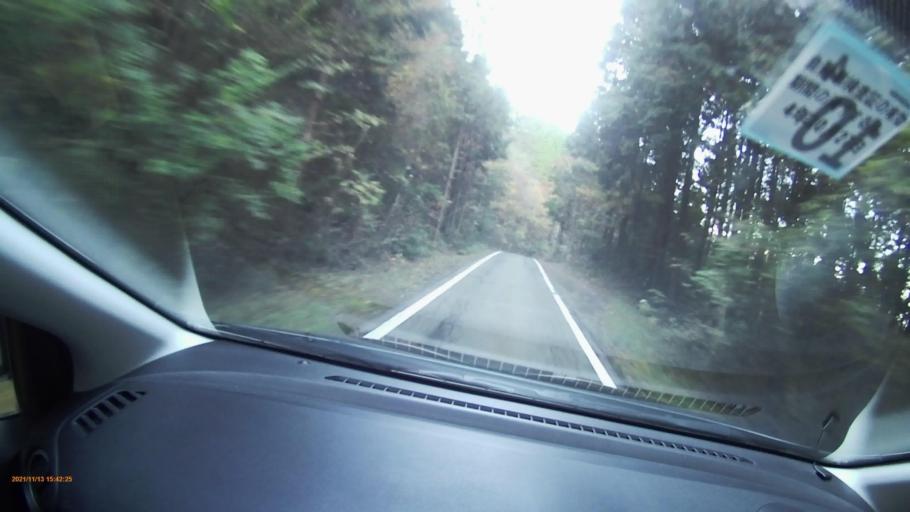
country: JP
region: Gifu
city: Nakatsugawa
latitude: 35.5922
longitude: 137.3918
